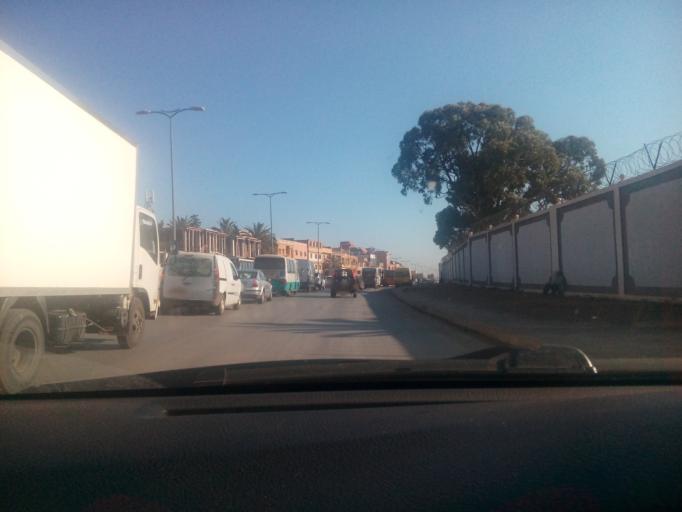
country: DZ
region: Oran
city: Oran
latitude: 35.6606
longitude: -0.6938
